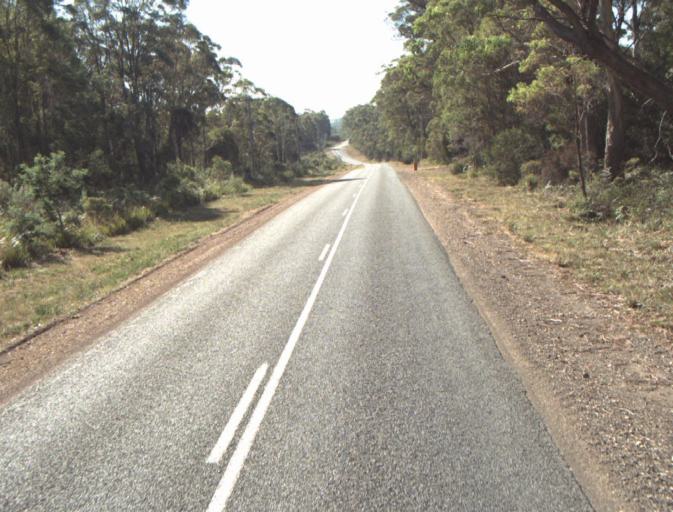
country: AU
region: Tasmania
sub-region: Launceston
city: Mayfield
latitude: -41.3077
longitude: 147.1335
